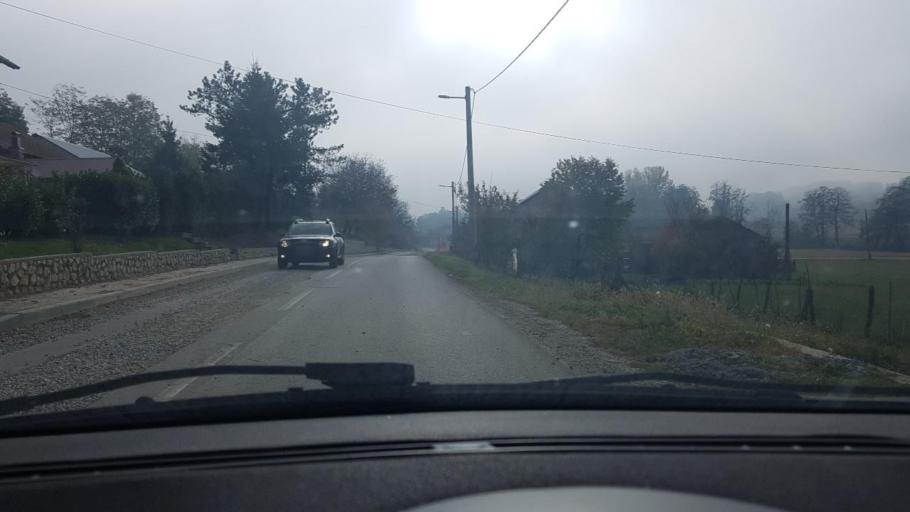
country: HR
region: Krapinsko-Zagorska
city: Zlatar
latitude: 46.1386
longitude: 16.0689
